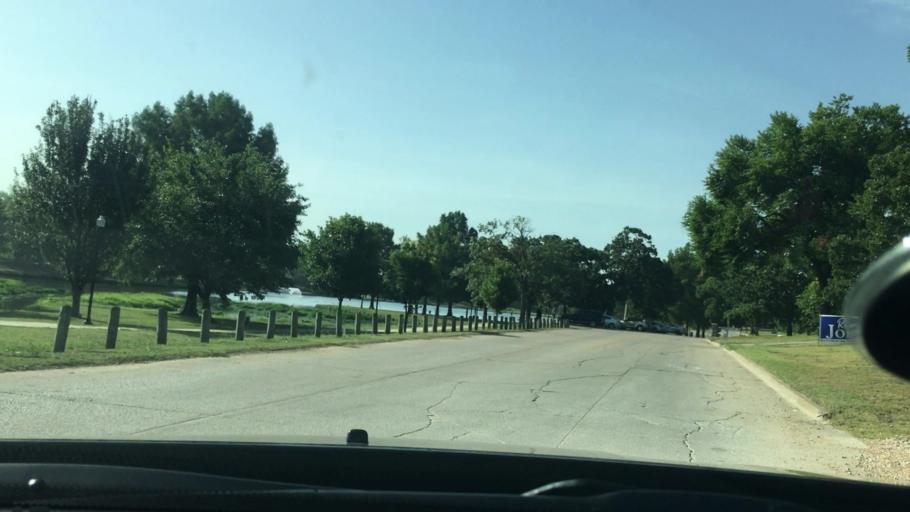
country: US
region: Oklahoma
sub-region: Pontotoc County
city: Ada
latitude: 34.7660
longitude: -96.6566
